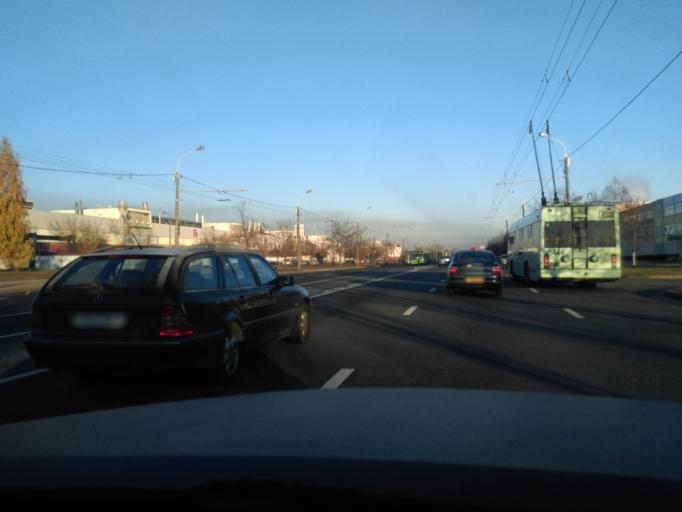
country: BY
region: Minsk
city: Minsk
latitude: 53.8962
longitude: 27.6425
